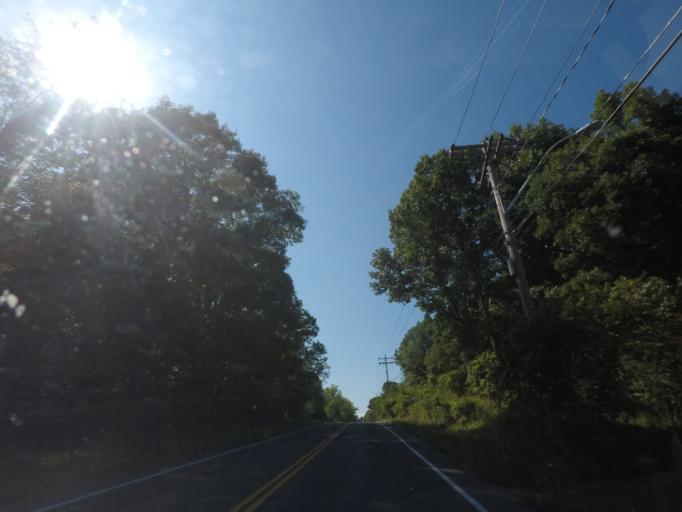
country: US
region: New York
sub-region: Albany County
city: Menands
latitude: 42.7139
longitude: -73.7276
